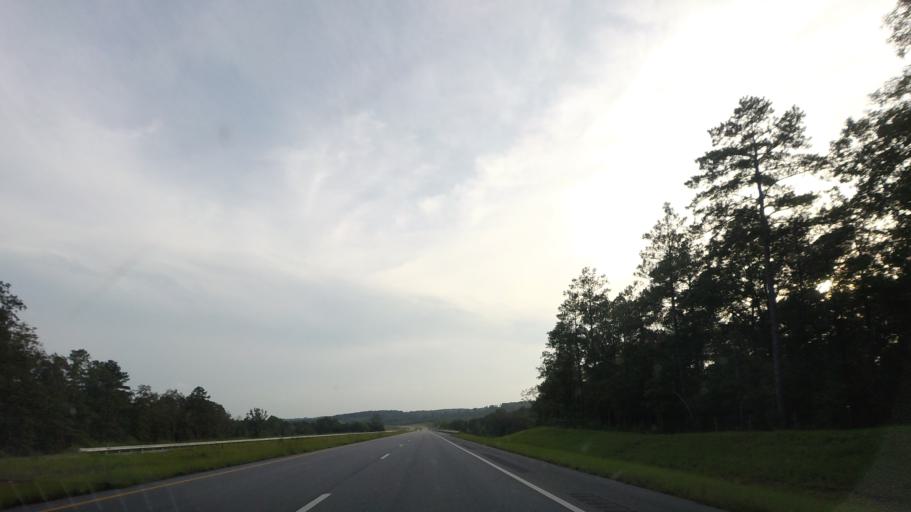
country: US
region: Georgia
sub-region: Wilkinson County
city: Gordon
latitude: 32.8902
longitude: -83.3650
